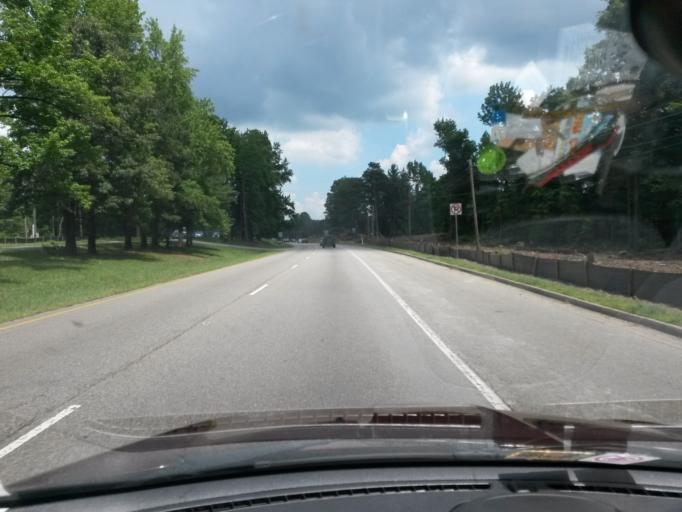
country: US
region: Virginia
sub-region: Chesterfield County
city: Enon
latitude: 37.3498
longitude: -77.3798
